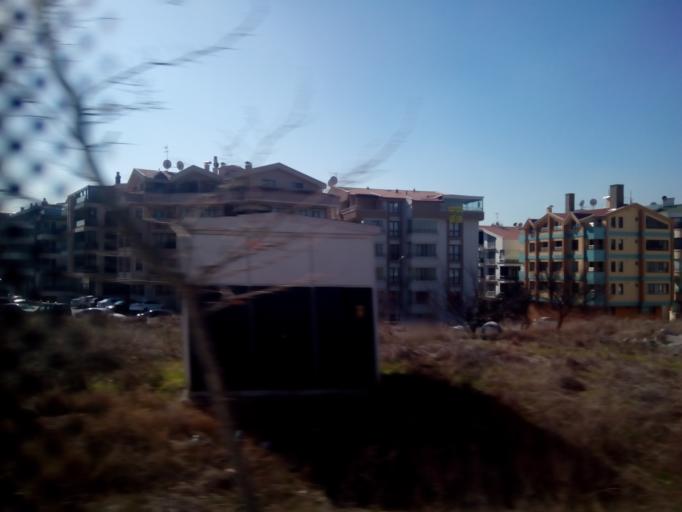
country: TR
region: Ankara
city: Batikent
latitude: 39.9167
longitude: 32.7715
